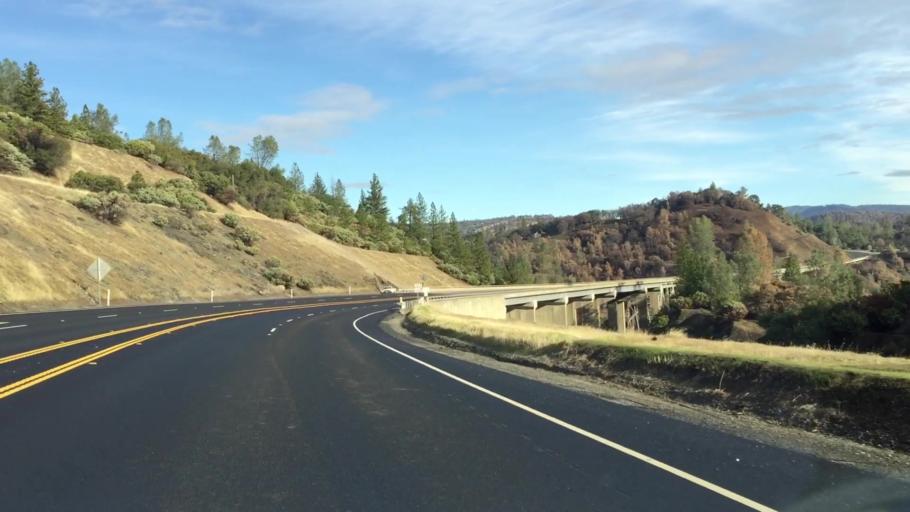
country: US
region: California
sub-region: Butte County
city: Paradise
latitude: 39.6606
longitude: -121.5356
